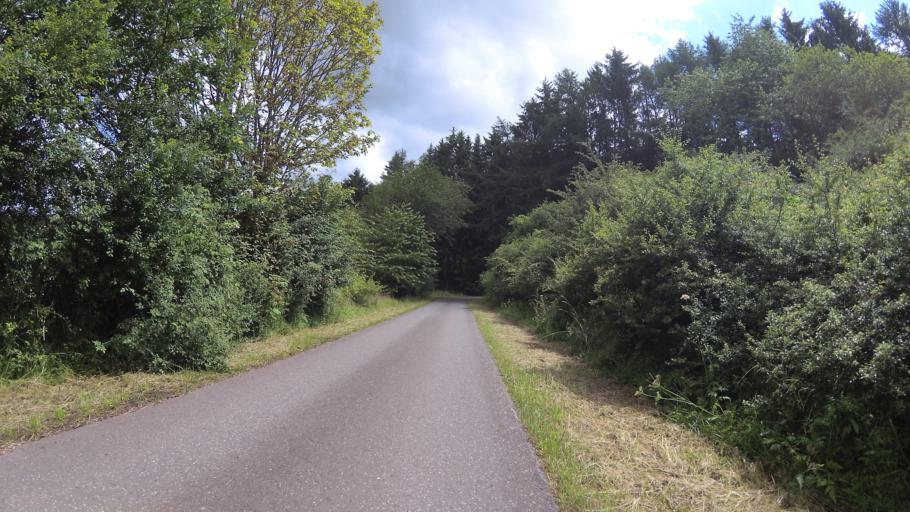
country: DE
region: Rheinland-Pfalz
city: Neuhutten
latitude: 49.5800
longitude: 7.0118
